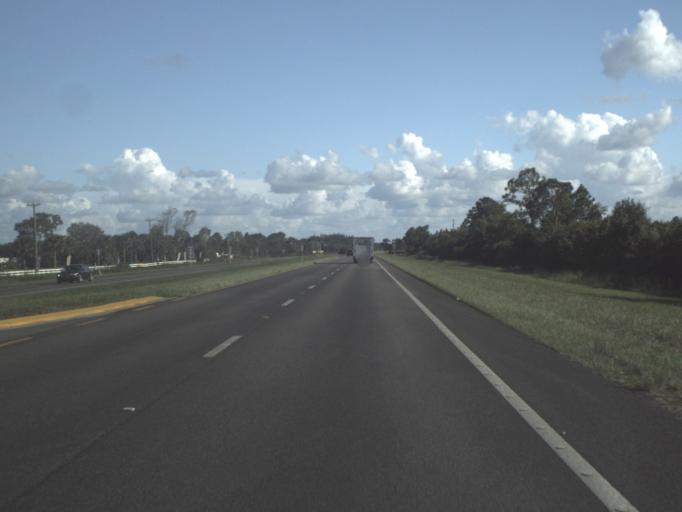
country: US
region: Florida
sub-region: Lee County
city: Suncoast Estates
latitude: 26.7731
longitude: -81.9333
